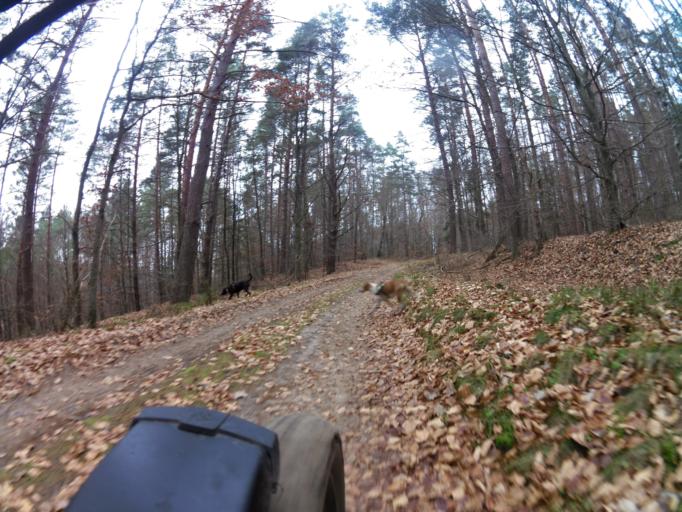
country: PL
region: West Pomeranian Voivodeship
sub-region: Powiat koszalinski
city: Polanow
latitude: 54.0453
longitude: 16.6588
